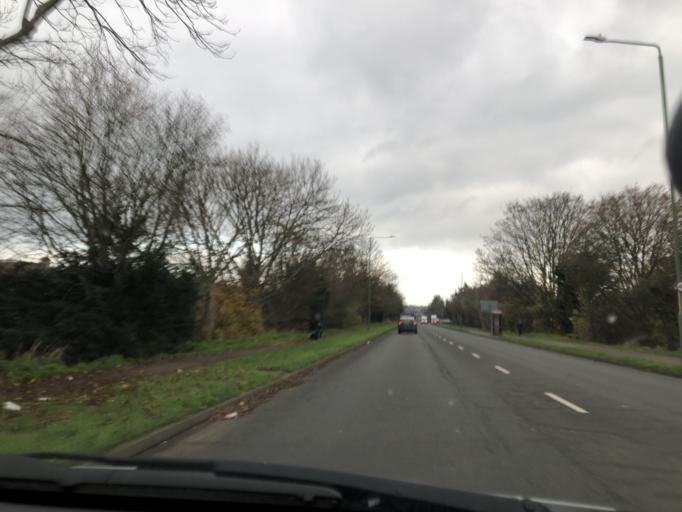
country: GB
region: England
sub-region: Kent
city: Dartford
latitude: 51.4453
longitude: 0.1927
